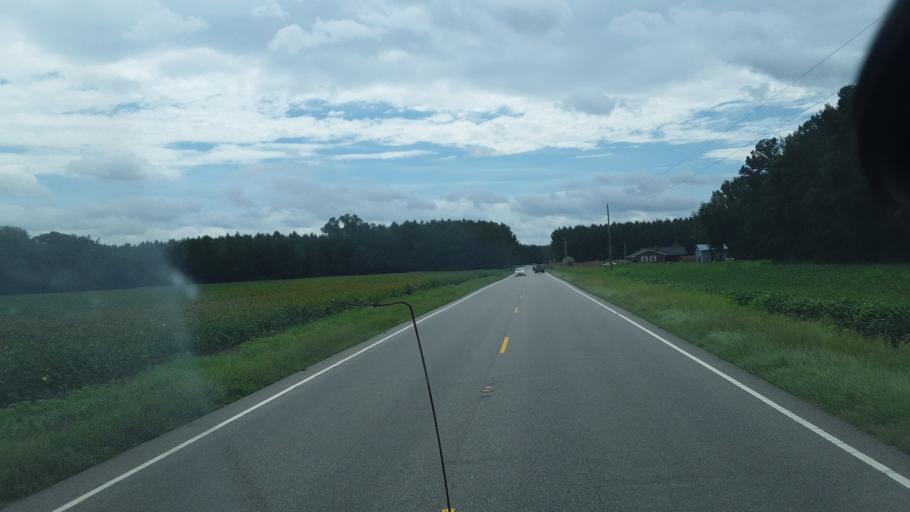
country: US
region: North Carolina
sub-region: Robeson County
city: Rowland
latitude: 34.6283
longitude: -79.3376
